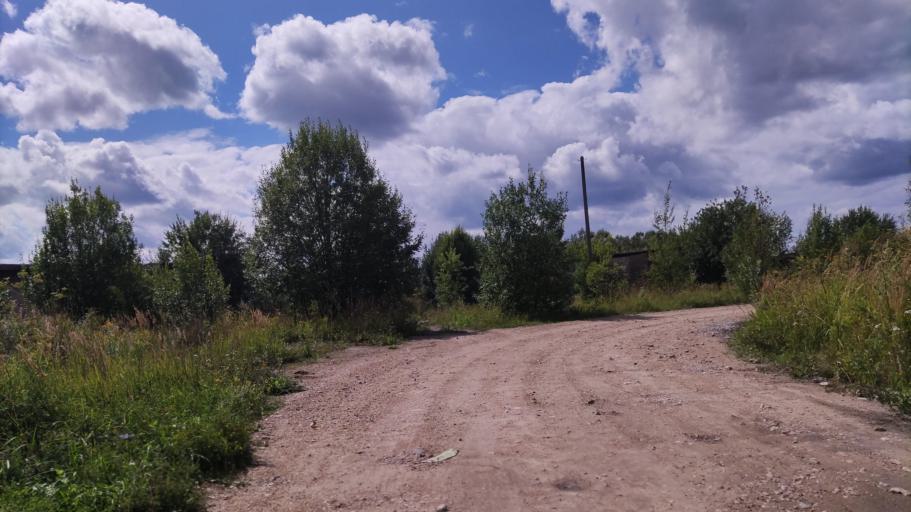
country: RU
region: Tverskaya
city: Rzhev
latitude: 56.2398
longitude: 34.3066
